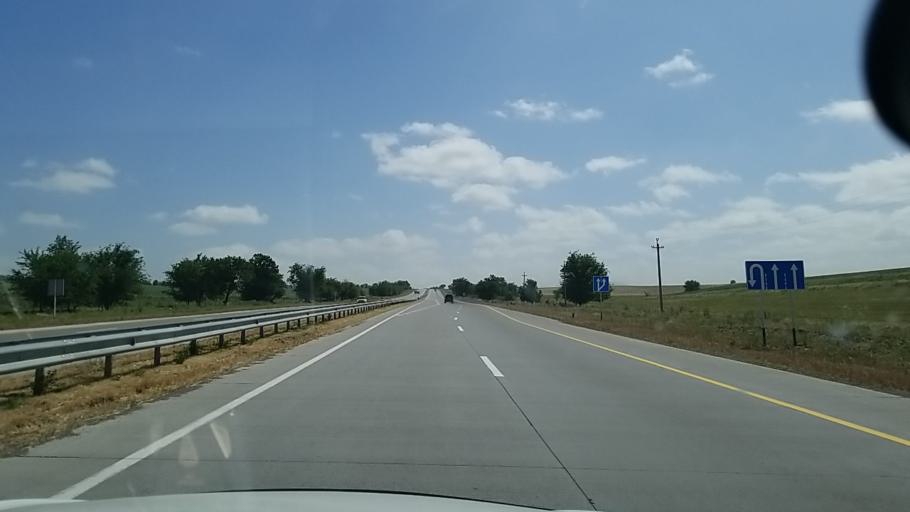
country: KZ
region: Ongtustik Qazaqstan
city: Sastobe
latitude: 42.4835
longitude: 69.9241
